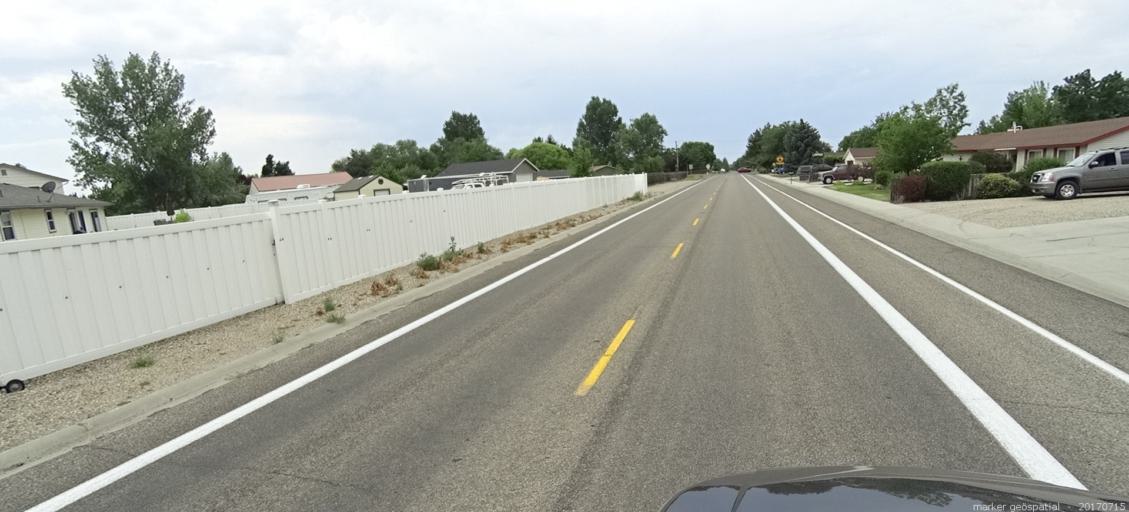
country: US
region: Idaho
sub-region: Ada County
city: Garden City
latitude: 43.5538
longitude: -116.2920
